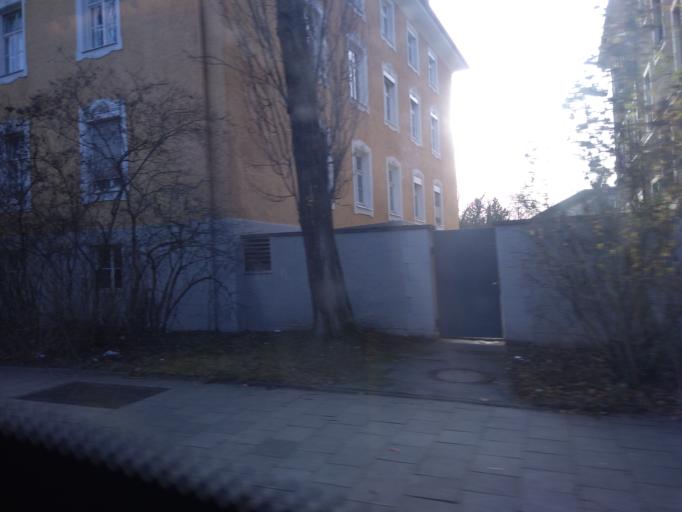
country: DE
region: Bavaria
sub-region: Upper Bavaria
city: Bogenhausen
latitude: 48.1652
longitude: 11.5928
